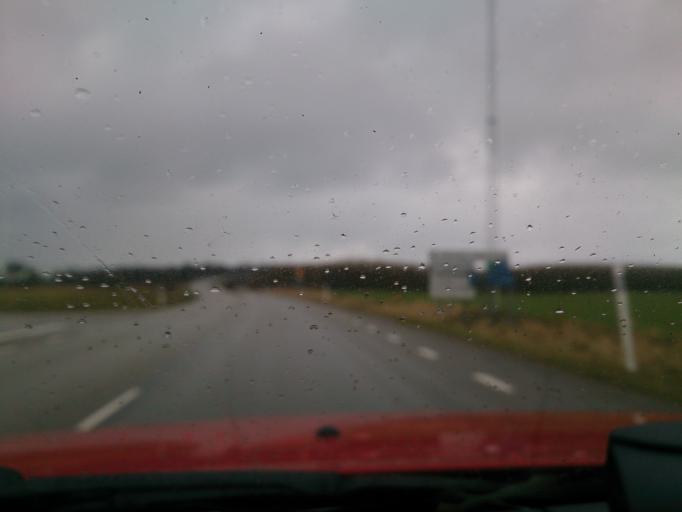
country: SE
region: Skane
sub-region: Ystads Kommun
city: Ystad
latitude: 55.4316
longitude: 13.7747
